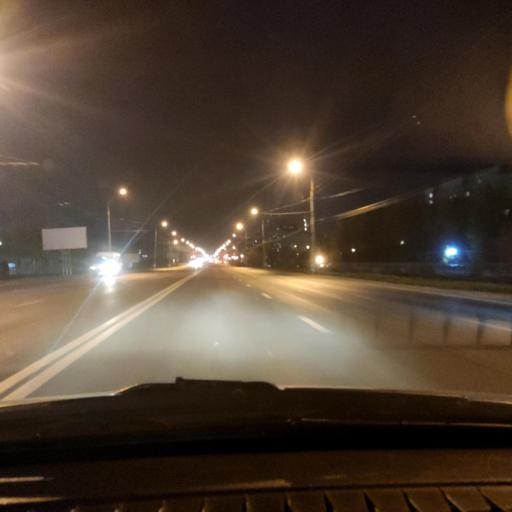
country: RU
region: Samara
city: Tol'yatti
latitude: 53.5474
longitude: 49.3555
